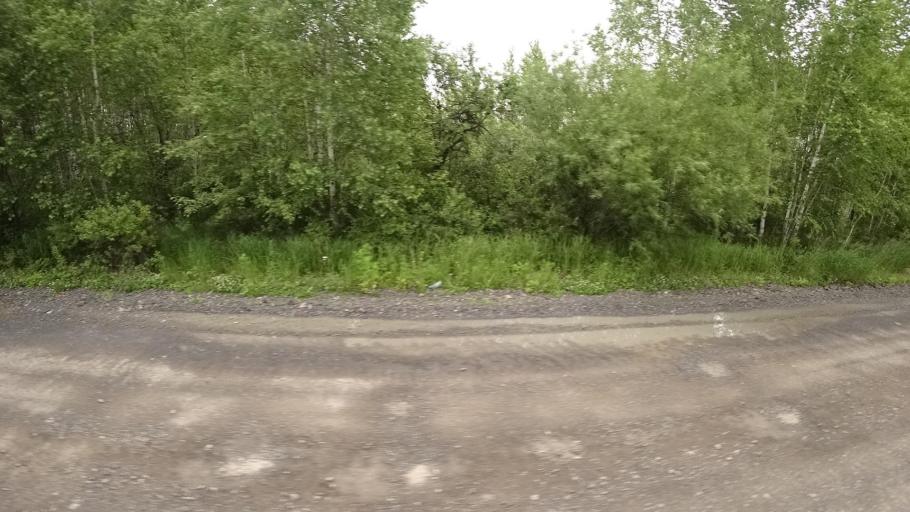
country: RU
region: Khabarovsk Krai
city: Amursk
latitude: 49.9041
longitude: 136.1387
